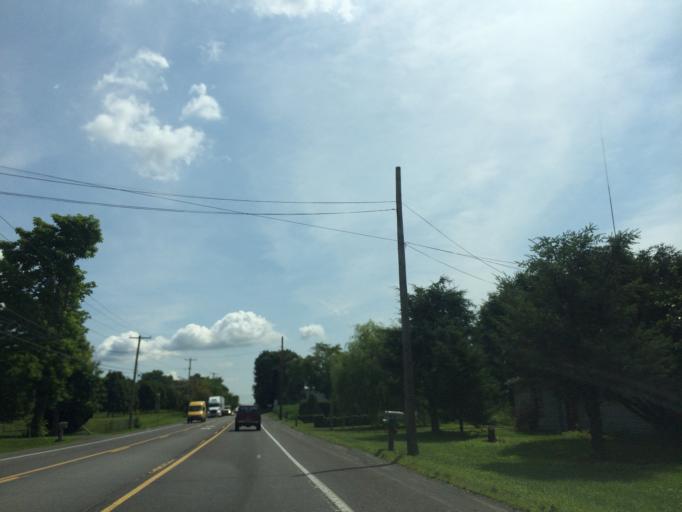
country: US
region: Pennsylvania
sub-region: Berks County
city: Topton
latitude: 40.5375
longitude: -75.7289
